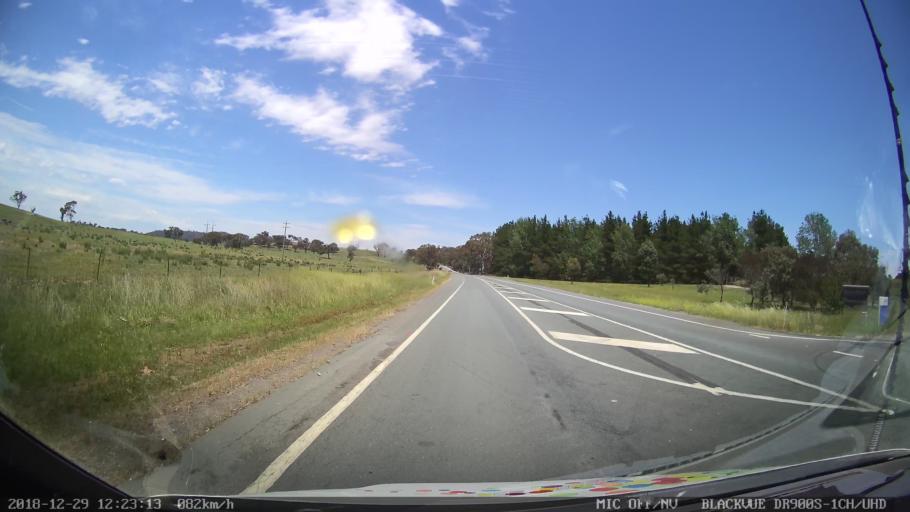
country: AU
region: New South Wales
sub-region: Queanbeyan
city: Queanbeyan
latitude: -35.4336
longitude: 149.2171
